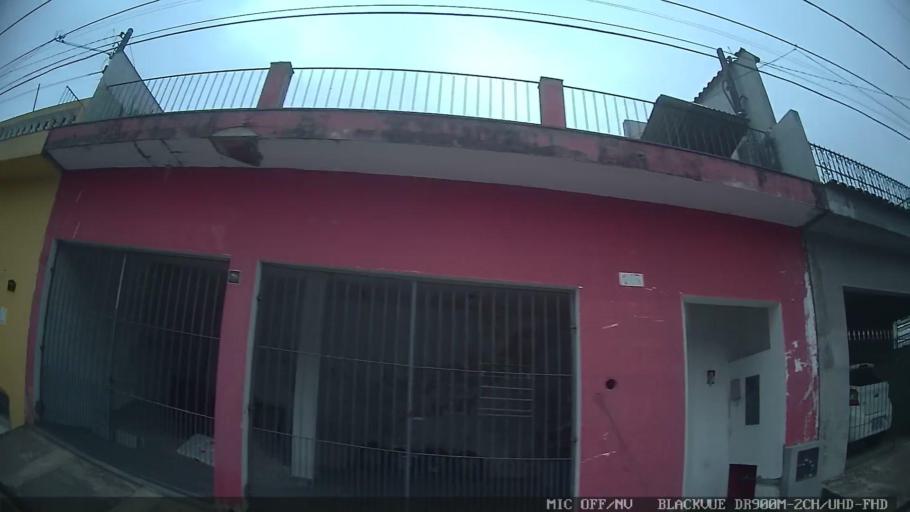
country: BR
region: Sao Paulo
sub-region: Mogi das Cruzes
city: Mogi das Cruzes
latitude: -23.5036
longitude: -46.1513
